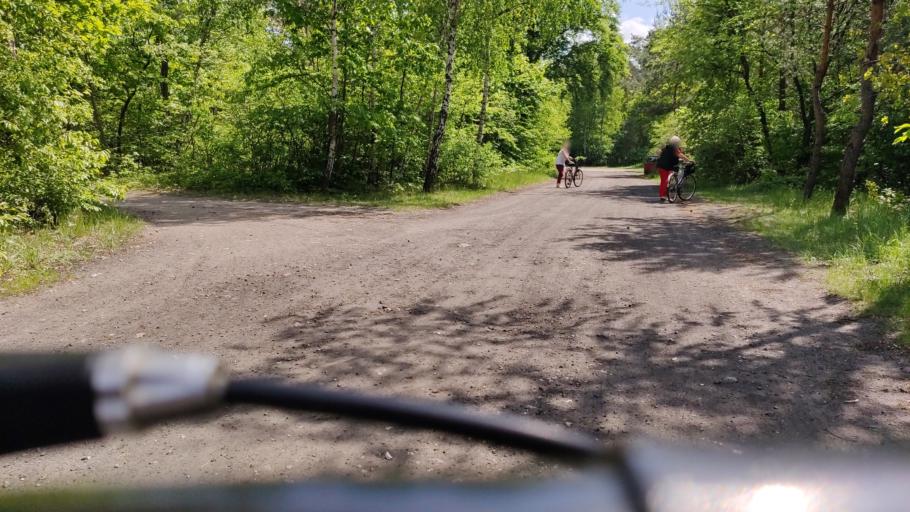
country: PL
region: Kujawsko-Pomorskie
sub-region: Wloclawek
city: Wloclawek
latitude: 52.6388
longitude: 19.0997
